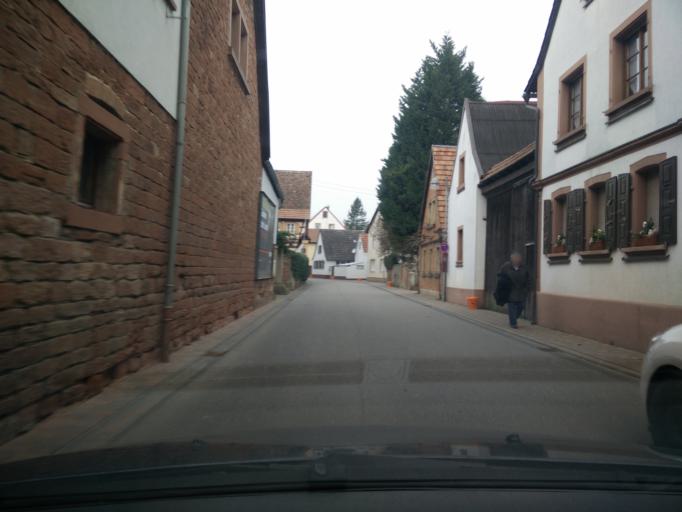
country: DE
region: Rheinland-Pfalz
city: Billigheim-Ingenheim
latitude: 49.1322
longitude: 8.0950
